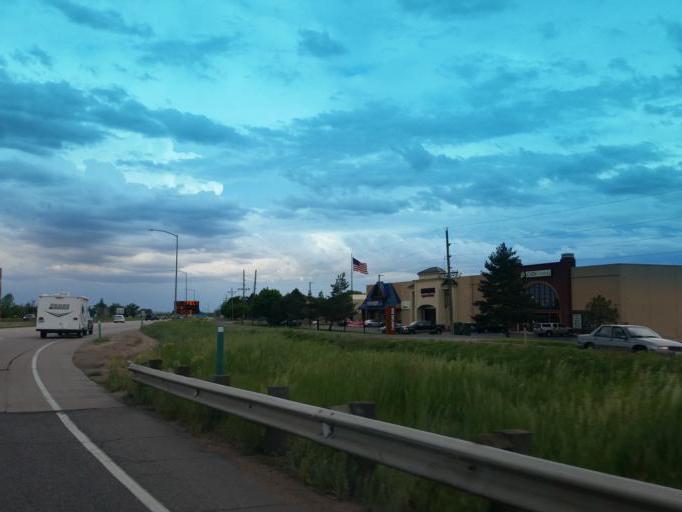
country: US
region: Colorado
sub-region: Larimer County
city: Fort Collins
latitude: 40.5792
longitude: -105.0017
